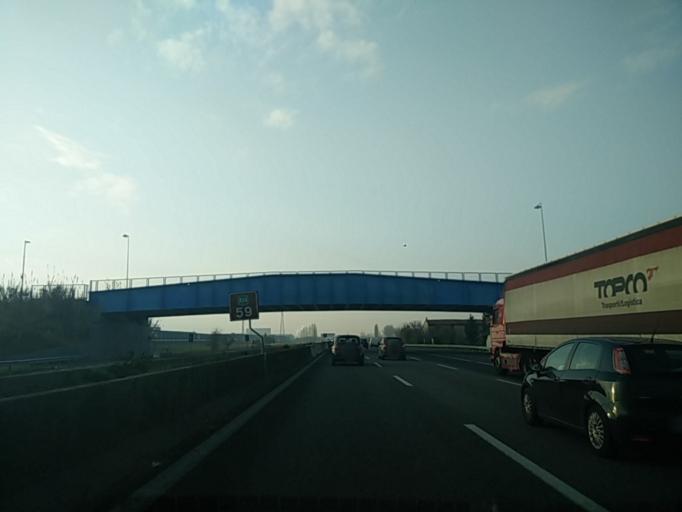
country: IT
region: Emilia-Romagna
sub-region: Provincia di Ravenna
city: Faenza
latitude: 44.3277
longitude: 11.8953
